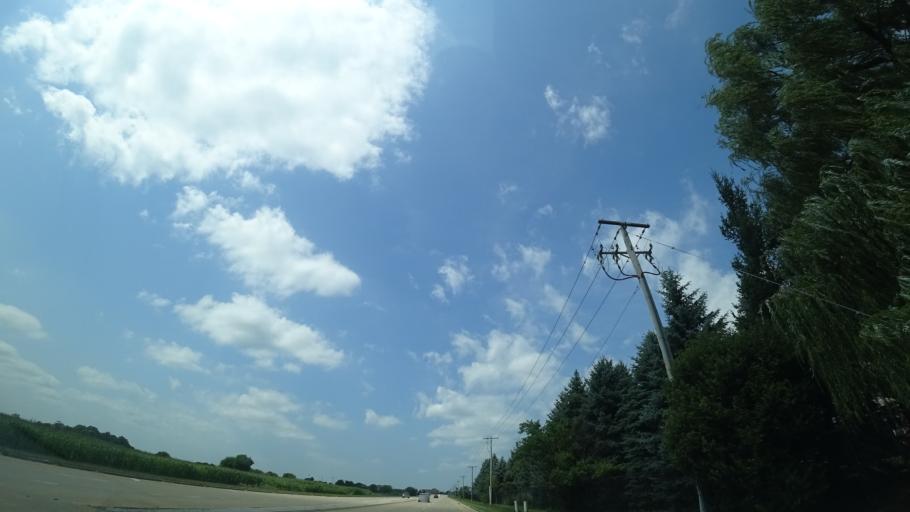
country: US
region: Illinois
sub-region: Will County
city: Frankfort Square
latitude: 41.5271
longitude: -87.7790
